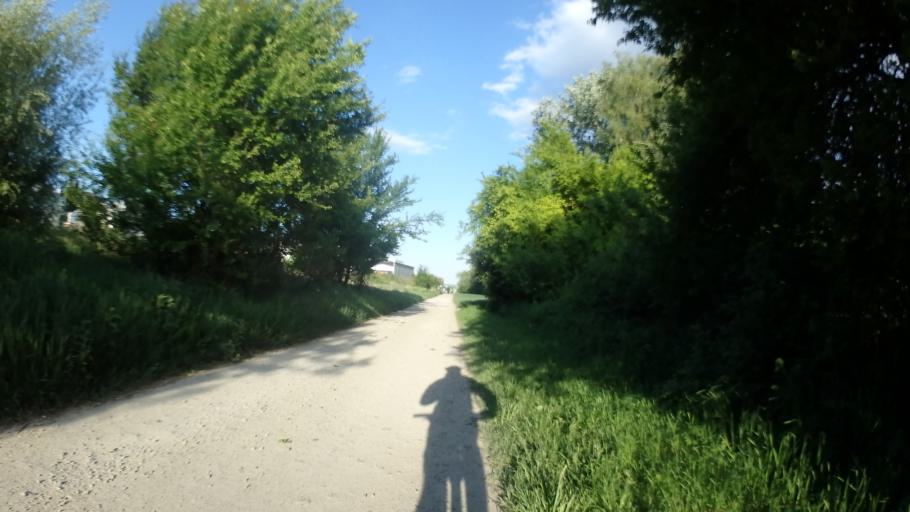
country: CZ
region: South Moravian
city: Moravany
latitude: 49.1441
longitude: 16.5864
